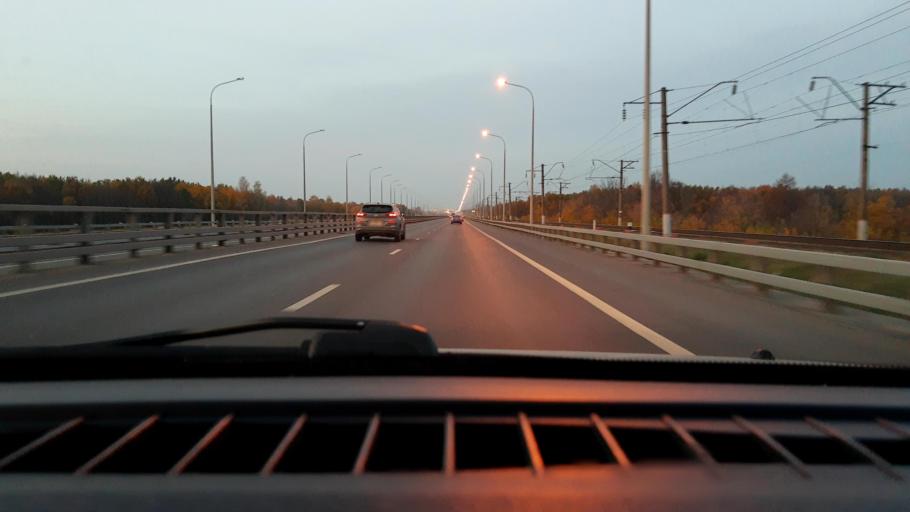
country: RU
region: Nizjnij Novgorod
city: Neklyudovo
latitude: 56.3823
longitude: 43.9606
